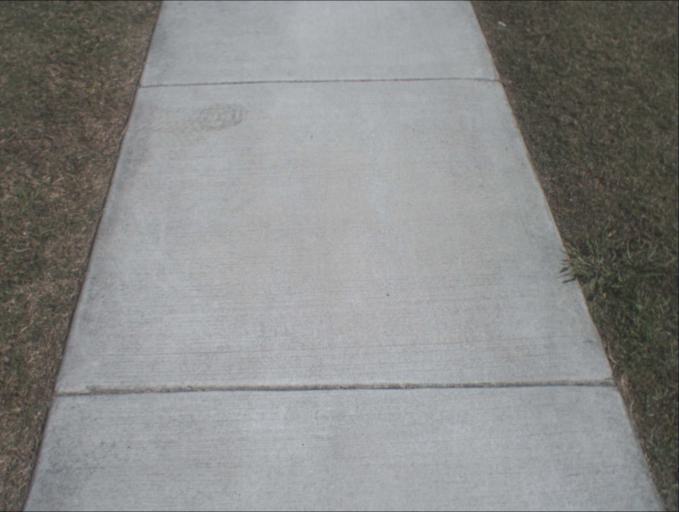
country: AU
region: Queensland
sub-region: Logan
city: Logan City
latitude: -27.6687
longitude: 153.0932
